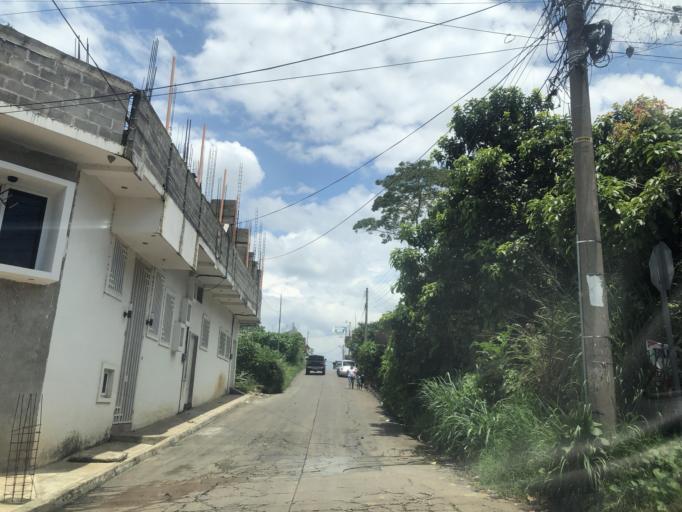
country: GT
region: Quetzaltenango
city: Coatepeque
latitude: 14.7088
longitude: -91.8679
